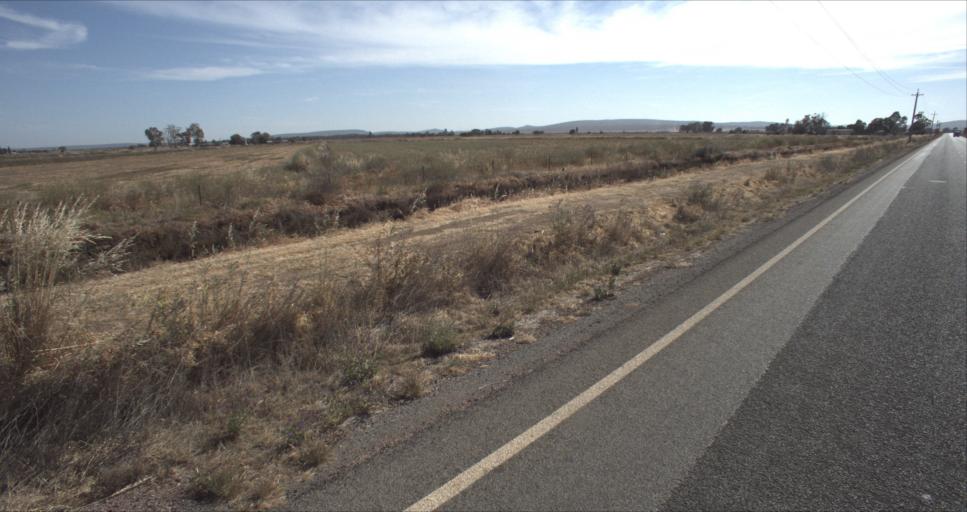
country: AU
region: New South Wales
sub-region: Leeton
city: Leeton
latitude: -34.5588
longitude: 146.4427
